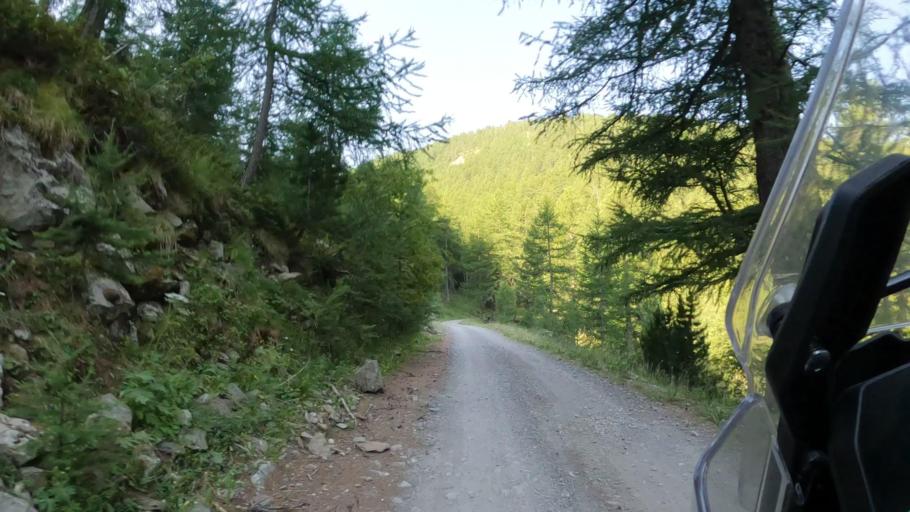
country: FR
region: Provence-Alpes-Cote d'Azur
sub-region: Departement des Hautes-Alpes
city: Guillestre
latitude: 44.5861
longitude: 6.6114
